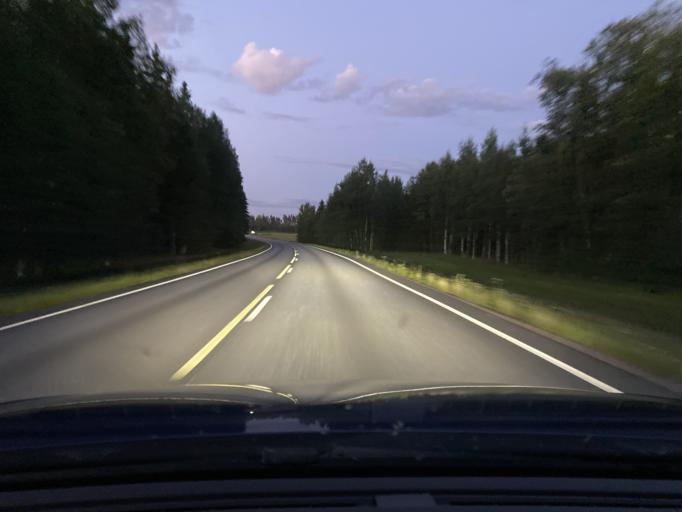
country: FI
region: Satakunta
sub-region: Pori
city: Vampula
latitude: 60.9498
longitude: 22.7199
